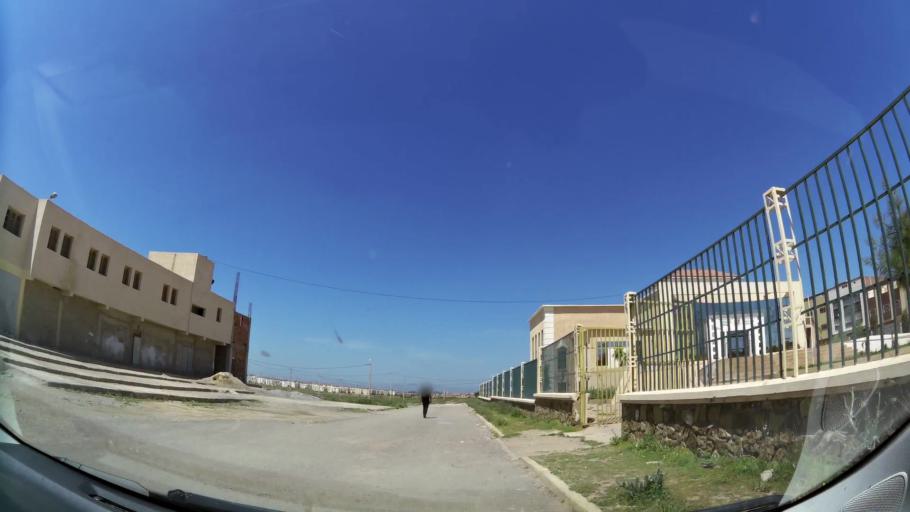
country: MA
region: Oriental
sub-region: Oujda-Angad
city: Oujda
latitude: 34.6908
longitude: -1.9313
